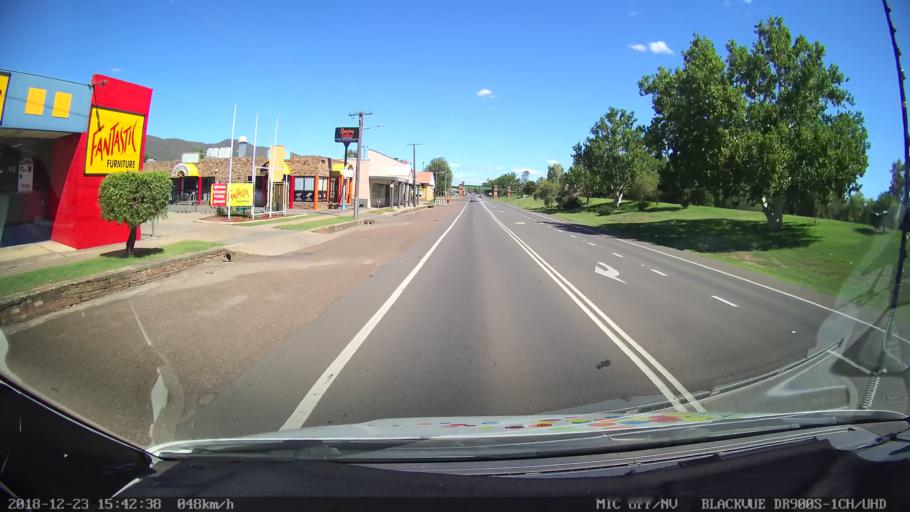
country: AU
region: New South Wales
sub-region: Tamworth Municipality
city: Tamworth
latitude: -31.0825
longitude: 150.9222
